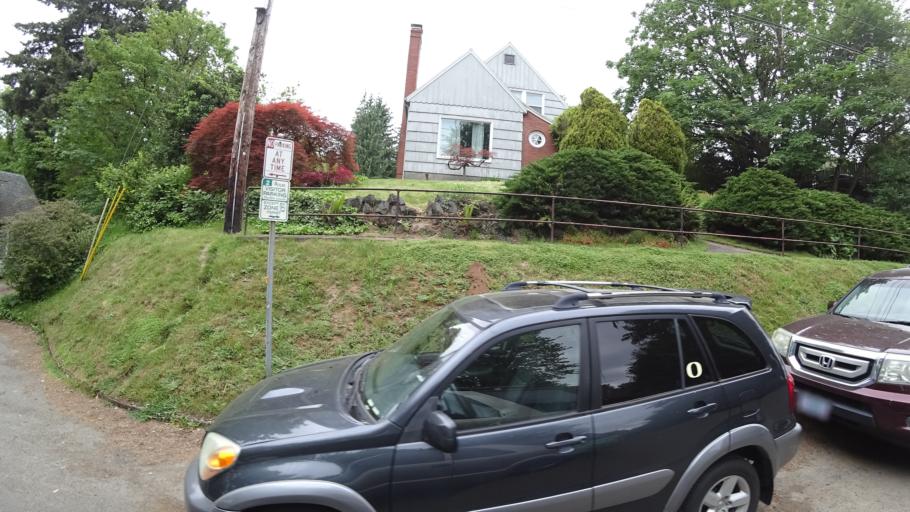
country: US
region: Oregon
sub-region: Multnomah County
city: Portland
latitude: 45.4985
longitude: -122.6903
